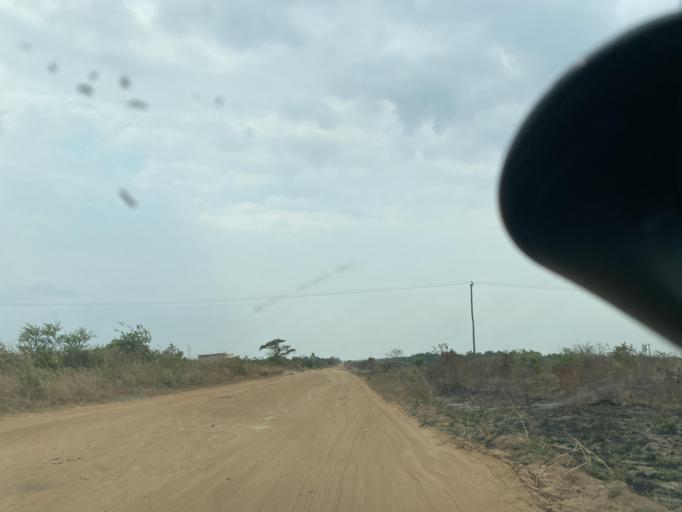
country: ZM
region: Lusaka
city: Lusaka
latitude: -15.2123
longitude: 28.3391
